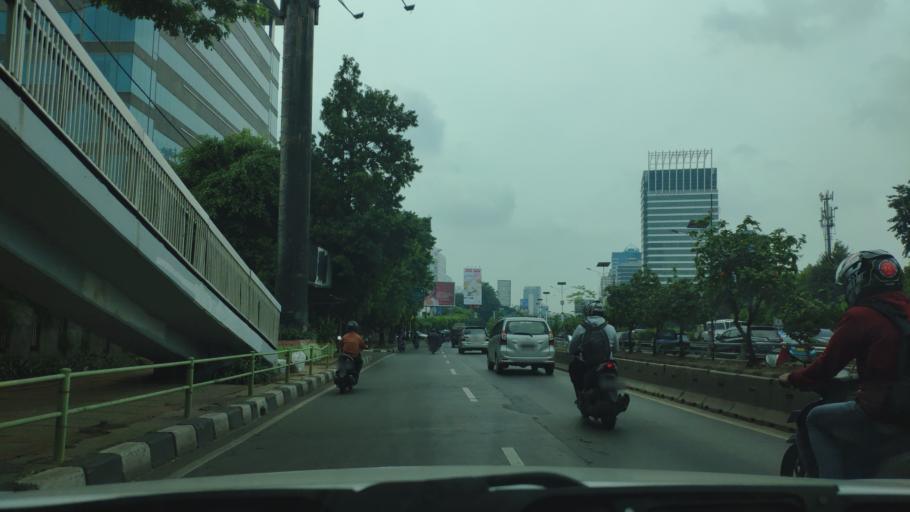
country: ID
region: Jakarta Raya
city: Jakarta
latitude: -6.1969
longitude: 106.7975
